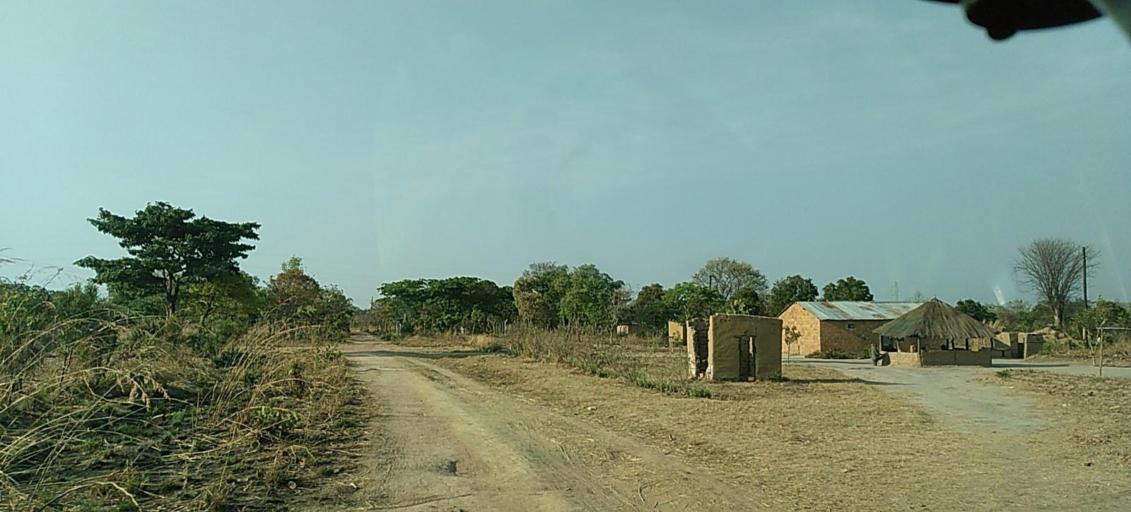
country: ZM
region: North-Western
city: Kalengwa
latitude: -13.1500
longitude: 25.0341
